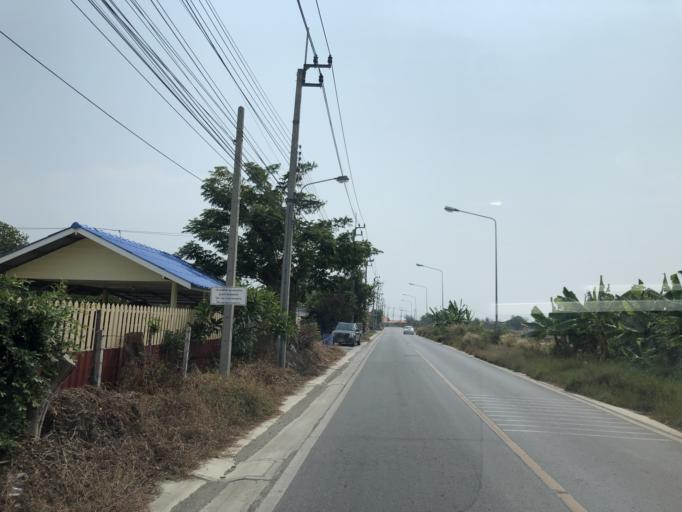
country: TH
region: Samut Prakan
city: Bang Bo
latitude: 13.5468
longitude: 100.8759
